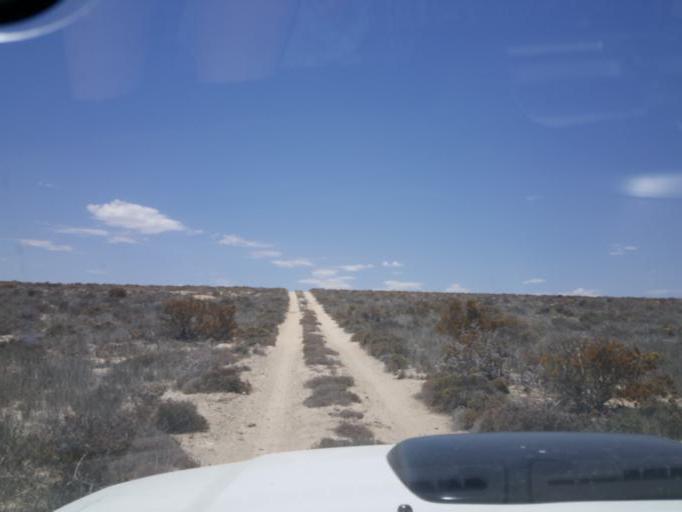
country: ZA
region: Northern Cape
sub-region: Namakwa District Municipality
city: Garies
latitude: -30.4815
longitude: 17.3625
